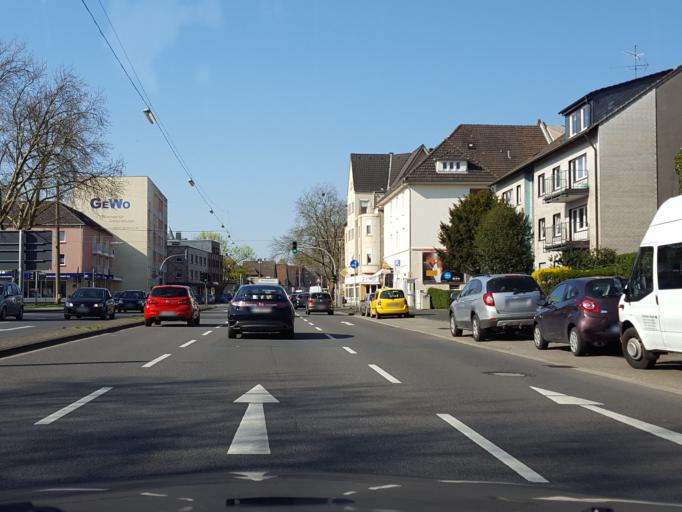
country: DE
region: North Rhine-Westphalia
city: Castrop-Rauxel
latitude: 51.5832
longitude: 7.3104
